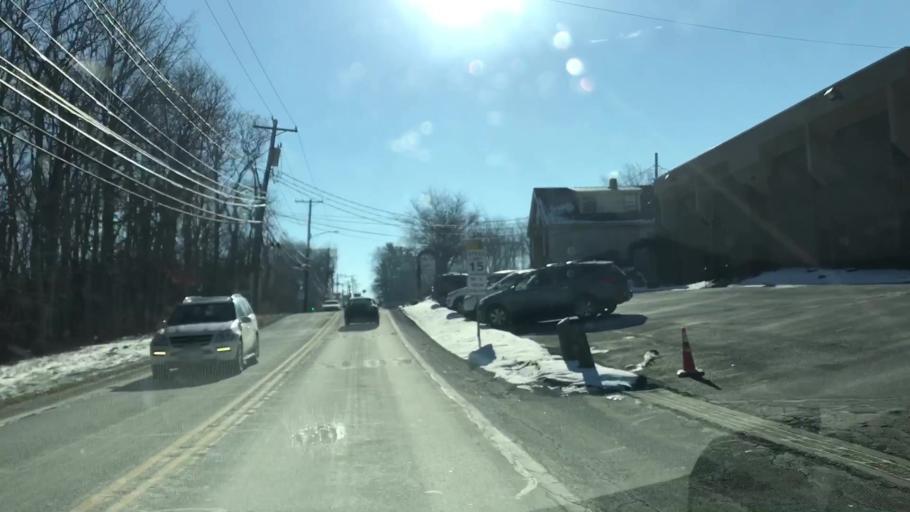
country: US
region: Pennsylvania
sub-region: Allegheny County
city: Carnot-Moon
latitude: 40.5134
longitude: -80.2164
